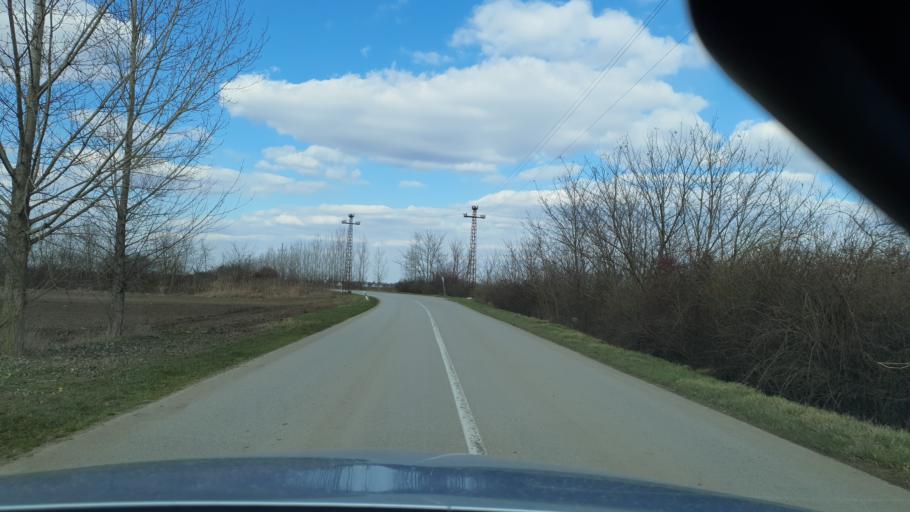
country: RS
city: Ravno Selo
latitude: 45.4315
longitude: 19.6053
